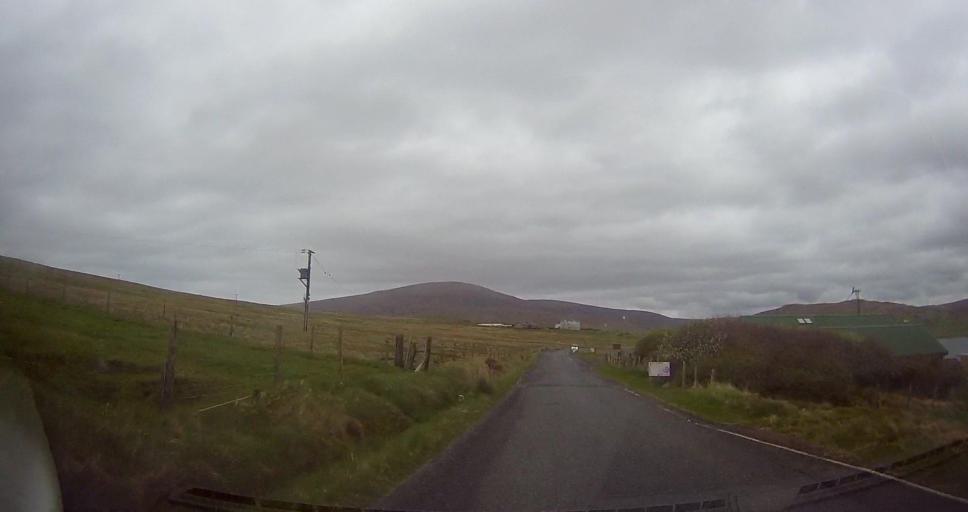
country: GB
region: Scotland
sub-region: Shetland Islands
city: Lerwick
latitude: 60.4872
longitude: -1.4675
